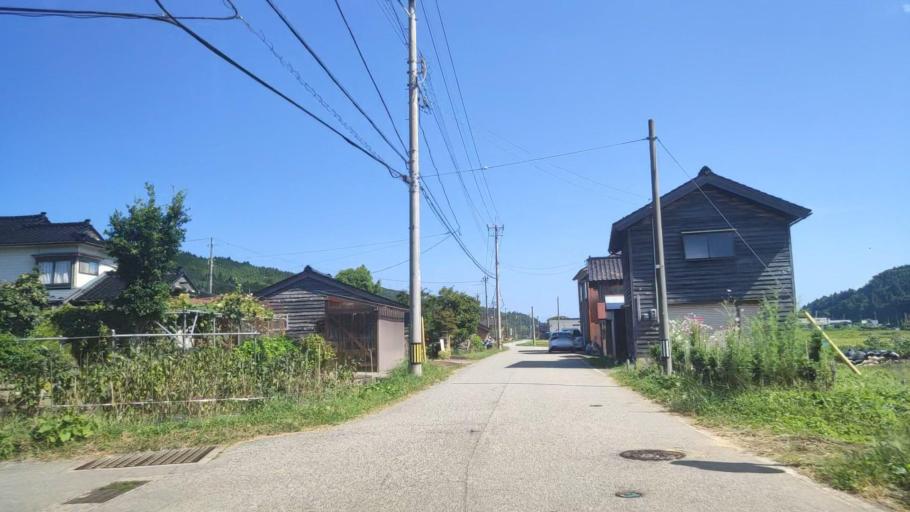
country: JP
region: Ishikawa
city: Nanao
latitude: 37.3752
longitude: 136.8760
